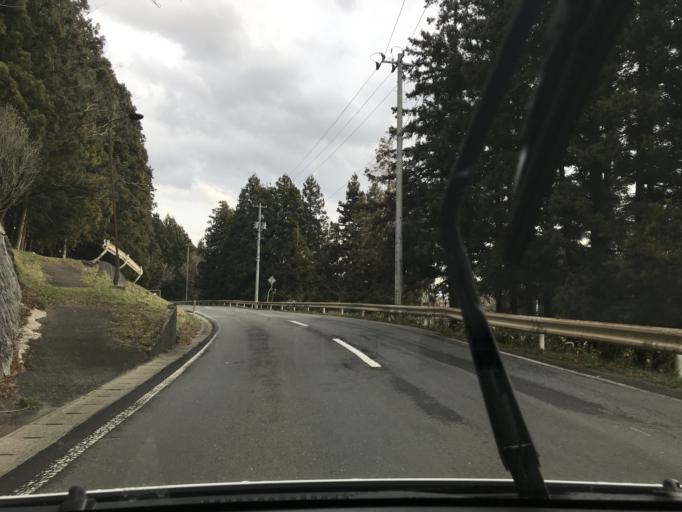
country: JP
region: Iwate
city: Mizusawa
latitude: 39.1131
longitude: 141.1875
